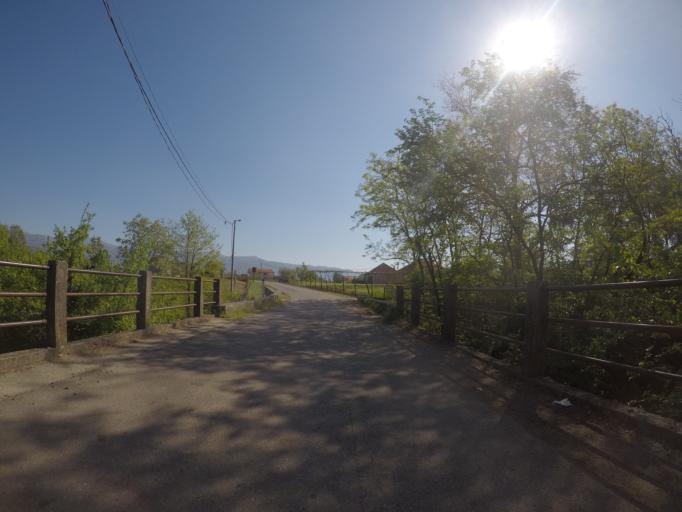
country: ME
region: Danilovgrad
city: Danilovgrad
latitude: 42.5381
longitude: 19.0906
